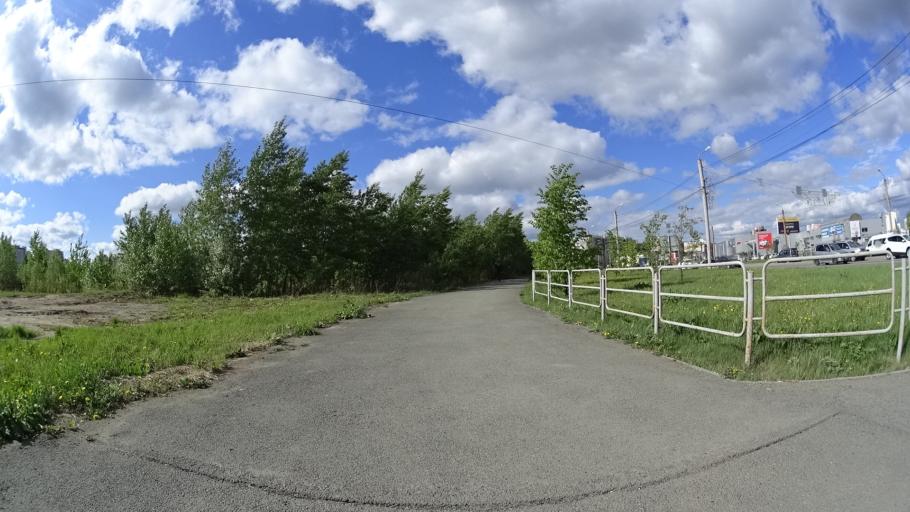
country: RU
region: Chelyabinsk
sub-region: Gorod Chelyabinsk
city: Chelyabinsk
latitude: 55.1673
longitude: 61.2945
